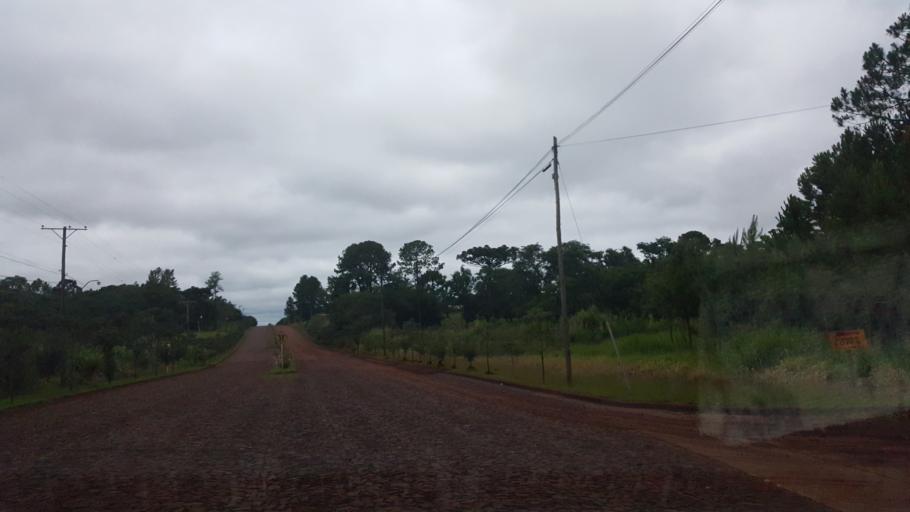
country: AR
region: Misiones
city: Ruiz de Montoya
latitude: -26.9619
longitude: -55.0566
